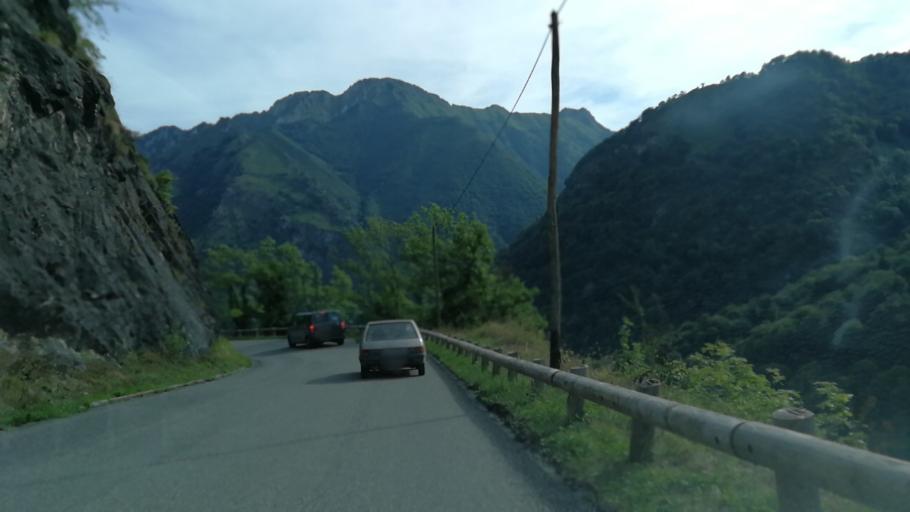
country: FR
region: Aquitaine
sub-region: Departement des Pyrenees-Atlantiques
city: Arette
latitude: 42.9350
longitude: -0.6256
